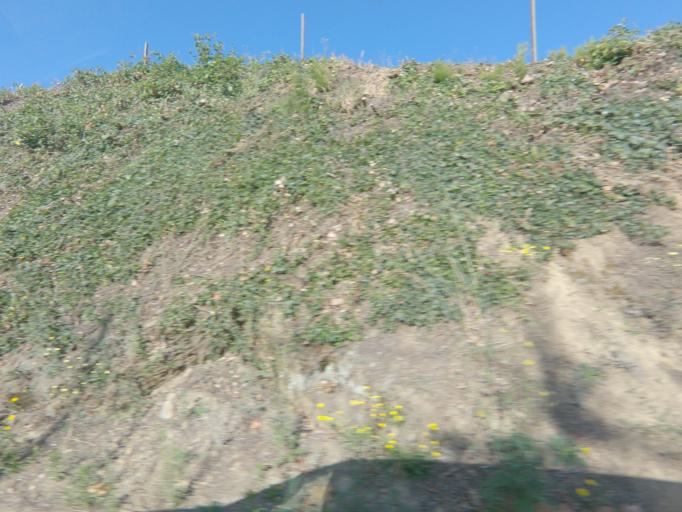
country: PT
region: Vila Real
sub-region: Sabrosa
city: Sabrosa
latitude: 41.2490
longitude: -7.5789
